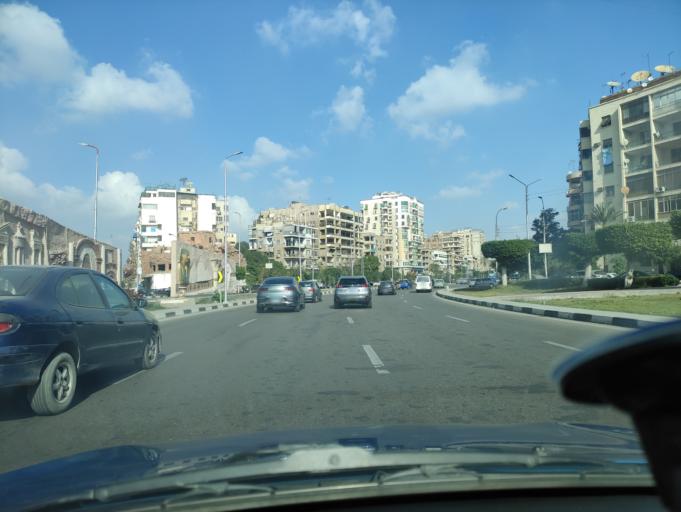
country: EG
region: Muhafazat al Qahirah
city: Cairo
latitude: 30.1000
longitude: 31.3432
